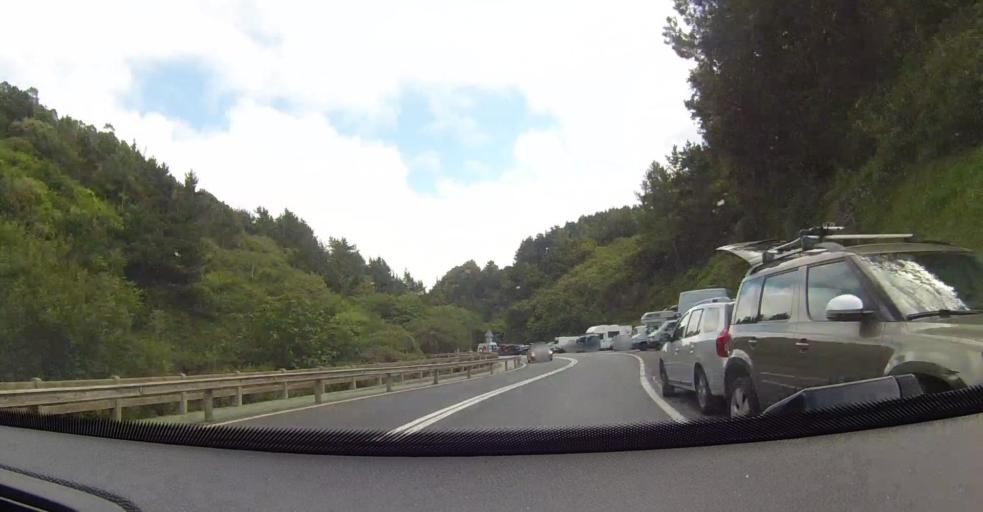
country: ES
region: Basque Country
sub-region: Bizkaia
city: Elantxobe
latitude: 43.4068
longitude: -2.6536
